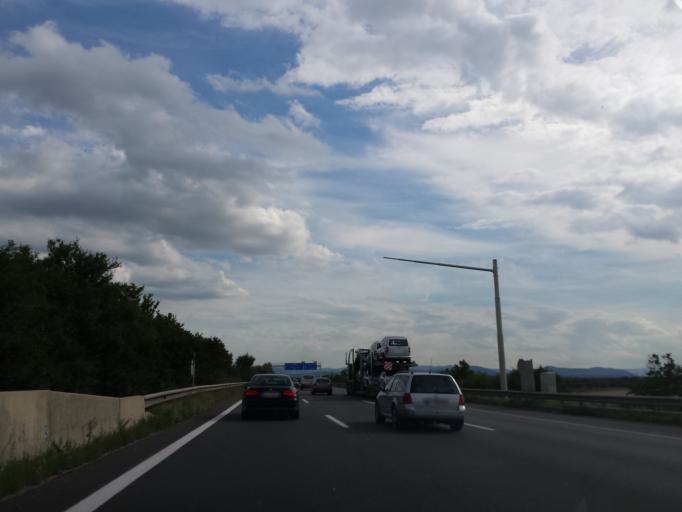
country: AT
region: Lower Austria
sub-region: Wiener Neustadt Stadt
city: Wiener Neustadt
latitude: 47.7939
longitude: 16.2034
